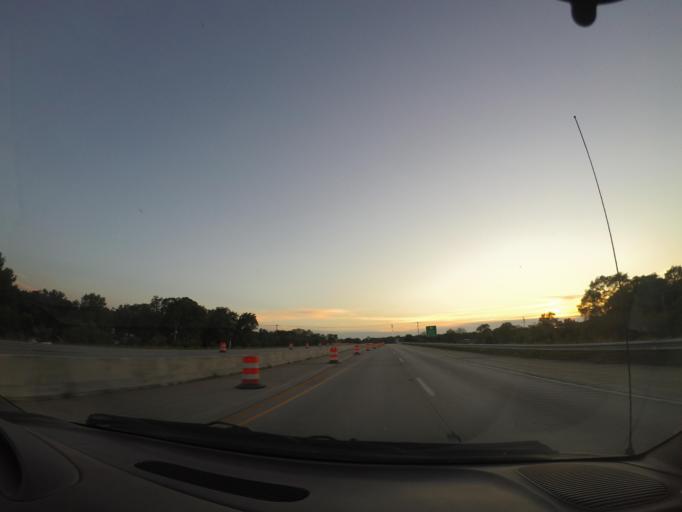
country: US
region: Indiana
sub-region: Elkhart County
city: Dunlap
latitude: 41.6572
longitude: -85.9197
